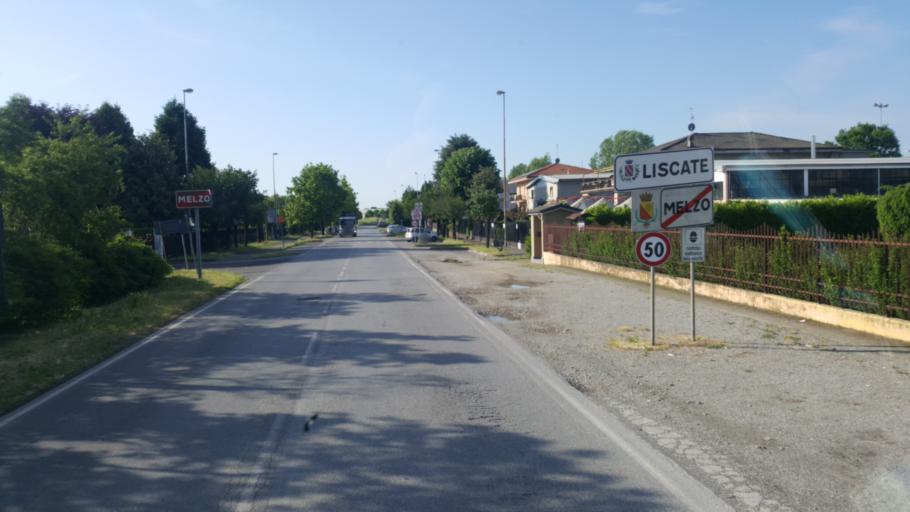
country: IT
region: Lombardy
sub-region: Citta metropolitana di Milano
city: Liscate
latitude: 45.4902
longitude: 9.4085
